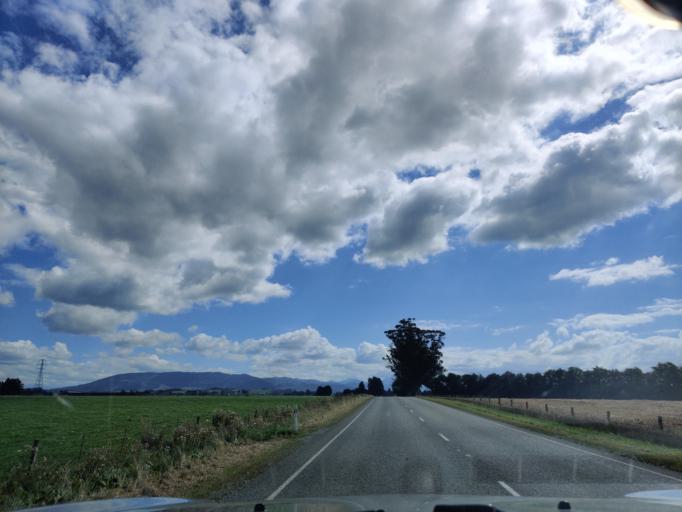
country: NZ
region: Canterbury
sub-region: Timaru District
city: Pleasant Point
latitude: -44.1240
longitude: 171.2463
